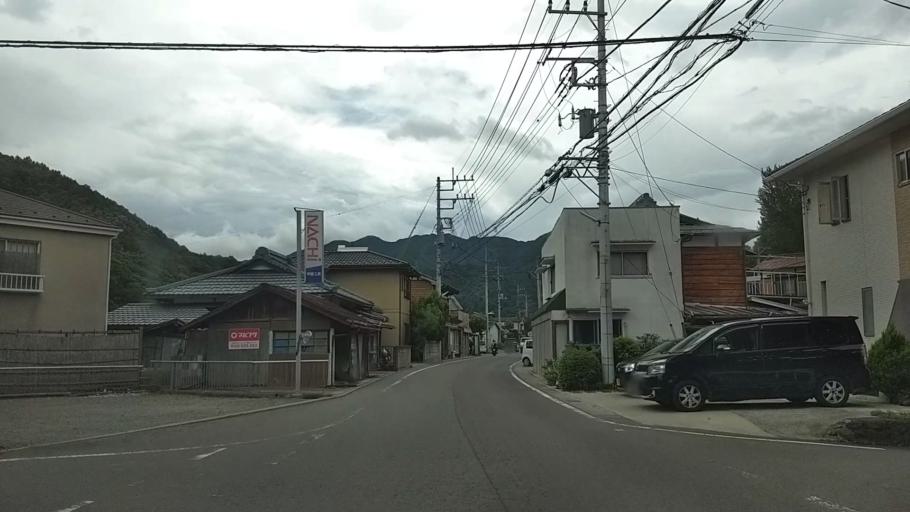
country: JP
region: Yamanashi
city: Otsuki
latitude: 35.5731
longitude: 138.9306
